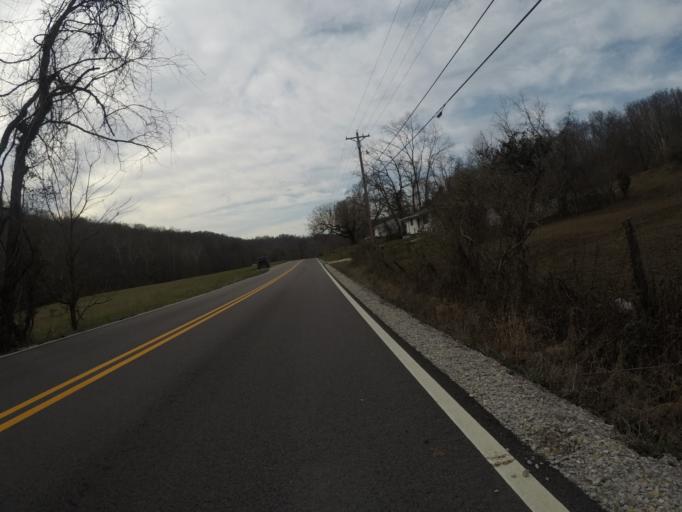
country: US
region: Ohio
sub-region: Lawrence County
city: Burlington
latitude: 38.4477
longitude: -82.5072
